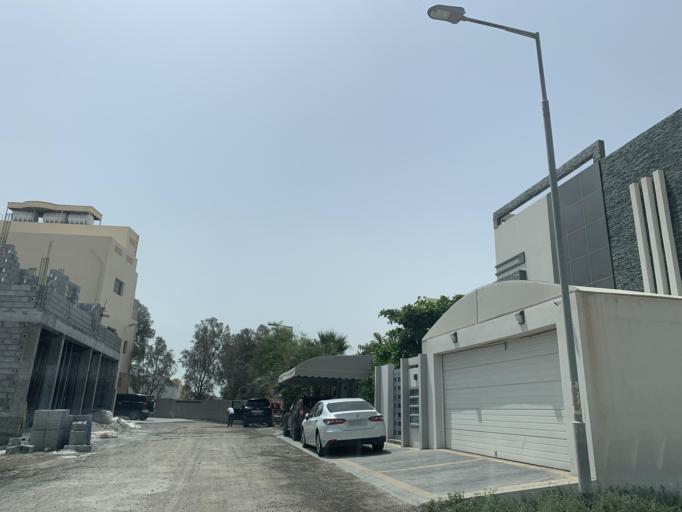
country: BH
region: Northern
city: Ar Rifa'
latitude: 26.1334
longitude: 50.5910
